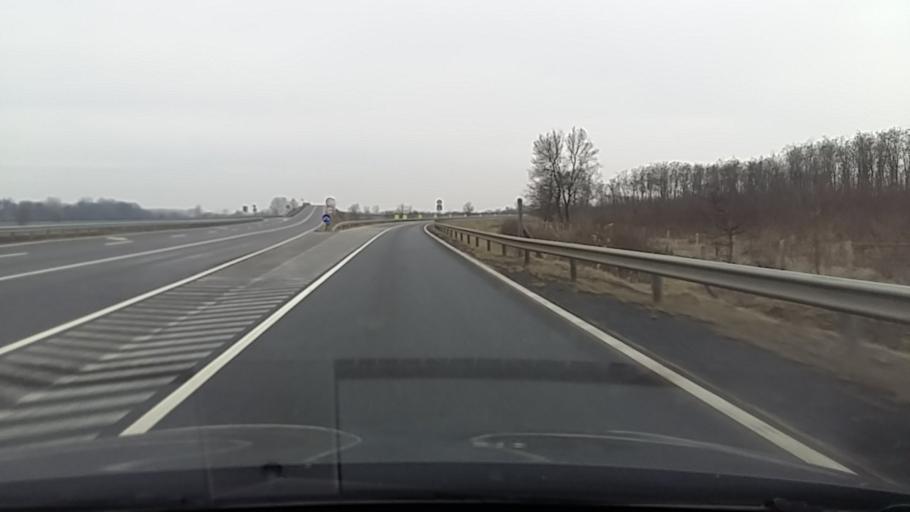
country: HU
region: Szabolcs-Szatmar-Bereg
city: Nagykallo
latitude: 47.9015
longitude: 21.8173
